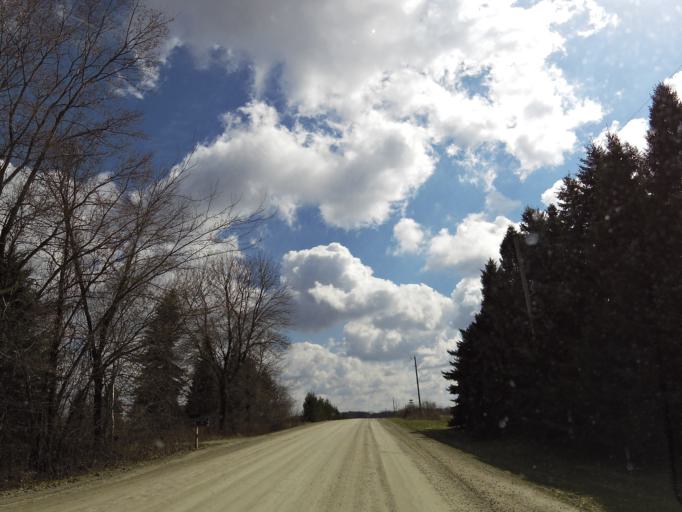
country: US
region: Minnesota
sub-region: Dodge County
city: Mantorville
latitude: 44.0732
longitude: -92.7182
